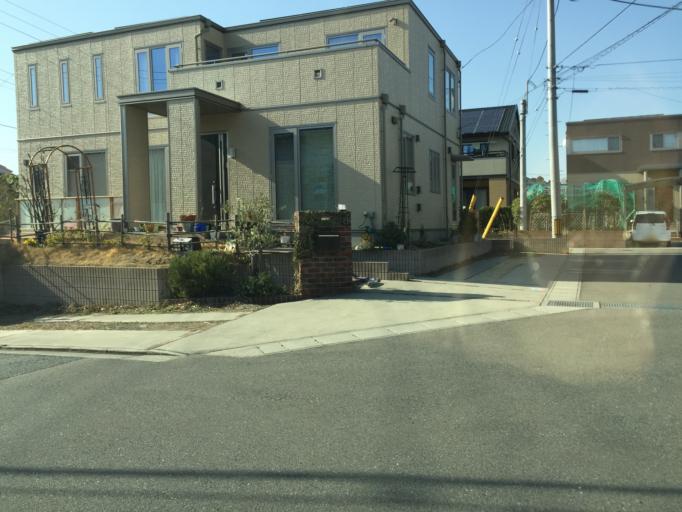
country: JP
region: Fukushima
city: Iwaki
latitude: 36.9637
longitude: 140.8699
